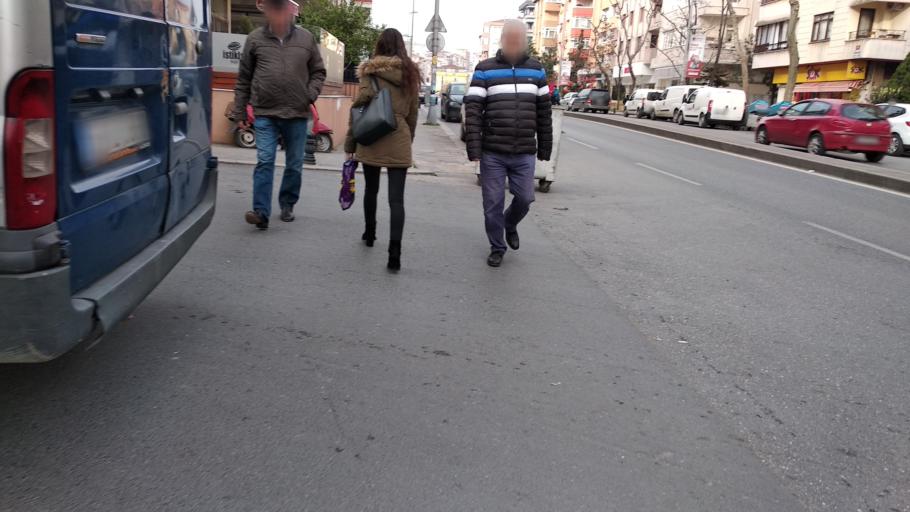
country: TR
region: Istanbul
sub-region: Atasehir
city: Atasehir
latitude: 40.9703
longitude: 29.1170
